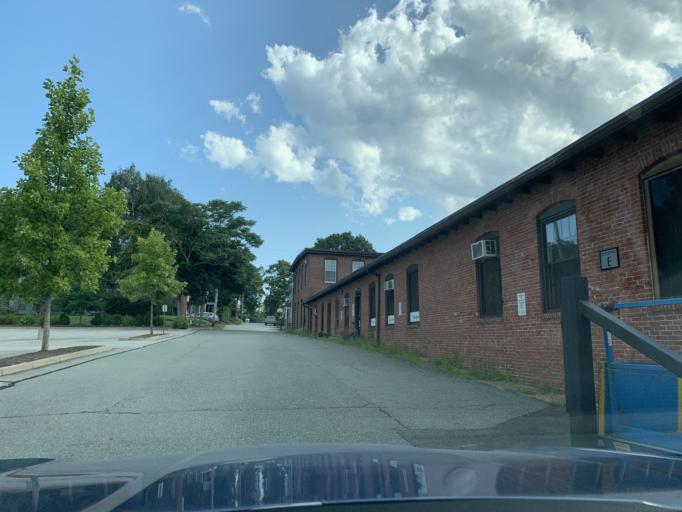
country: US
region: Rhode Island
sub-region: Kent County
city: East Greenwich
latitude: 41.6646
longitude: -71.4474
